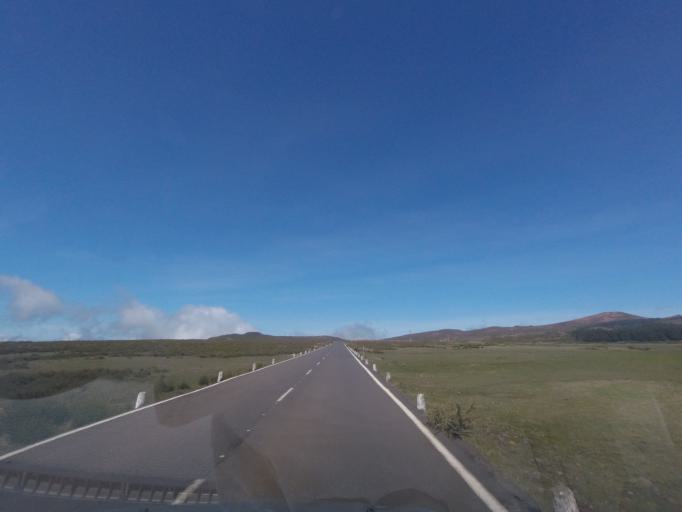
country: PT
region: Madeira
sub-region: Calheta
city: Arco da Calheta
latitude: 32.7499
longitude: -17.0984
